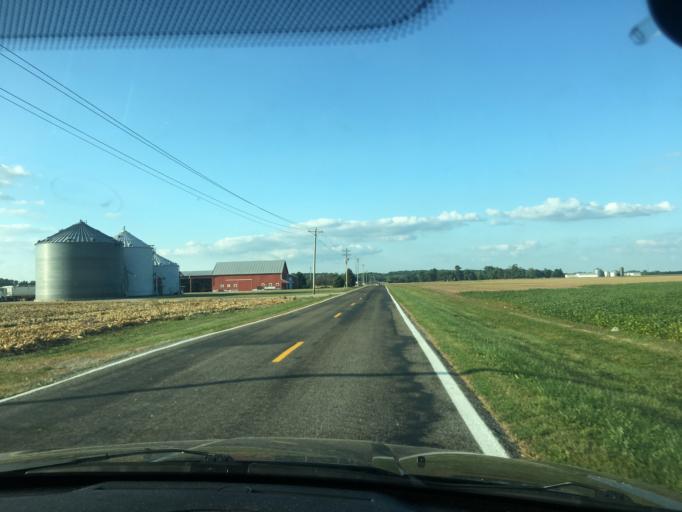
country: US
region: Ohio
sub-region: Logan County
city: West Liberty
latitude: 40.2053
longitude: -83.7795
